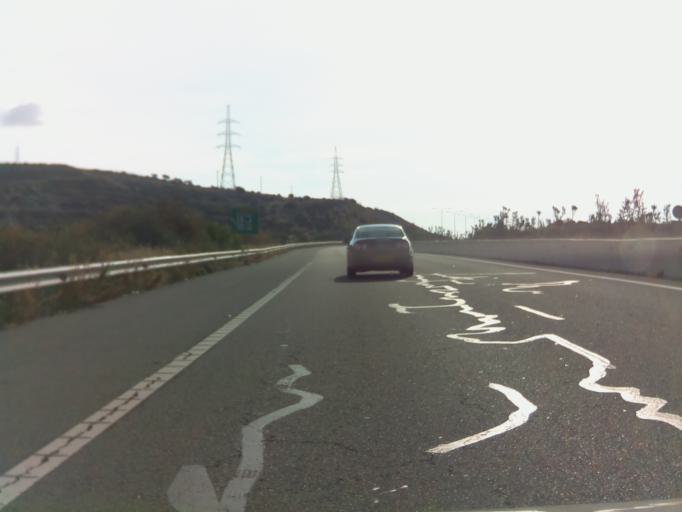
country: CY
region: Limassol
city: Pissouri
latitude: 34.6762
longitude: 32.6059
